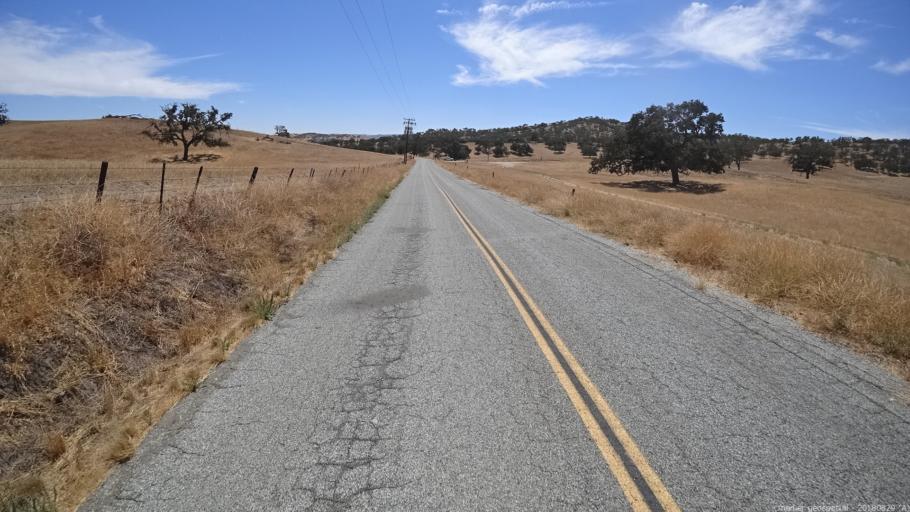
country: US
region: California
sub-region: San Luis Obispo County
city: Lake Nacimiento
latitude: 35.8299
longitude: -120.8450
